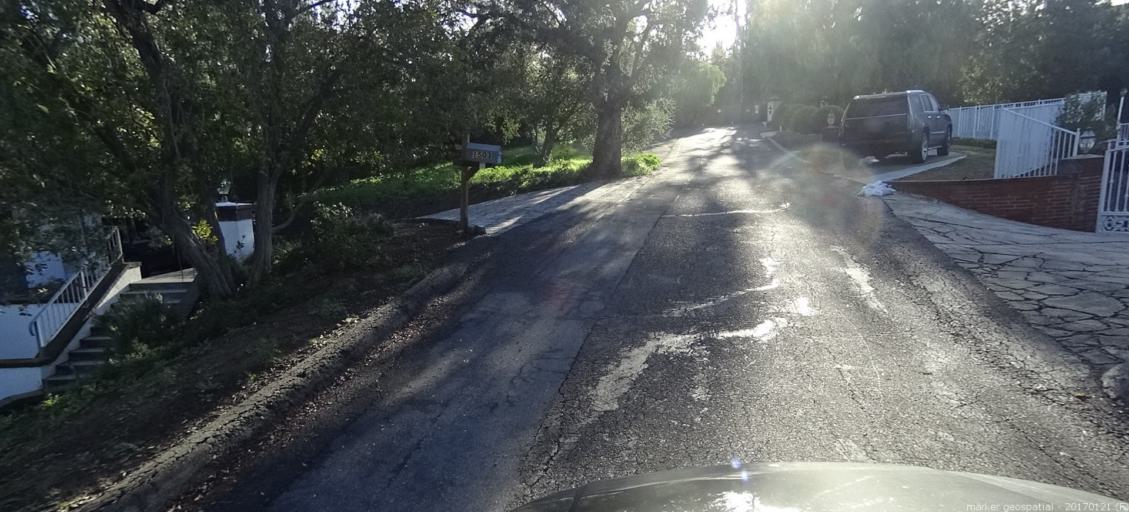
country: US
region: California
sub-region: Orange County
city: North Tustin
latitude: 33.7589
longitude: -117.7887
